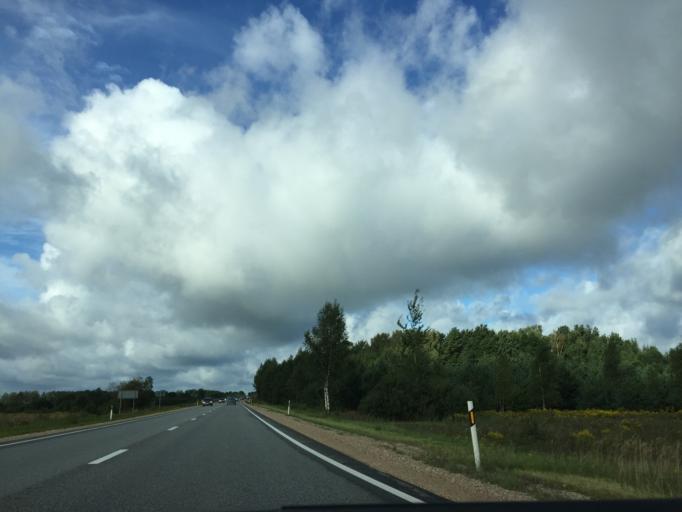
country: LV
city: Tireli
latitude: 56.9286
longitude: 23.6297
